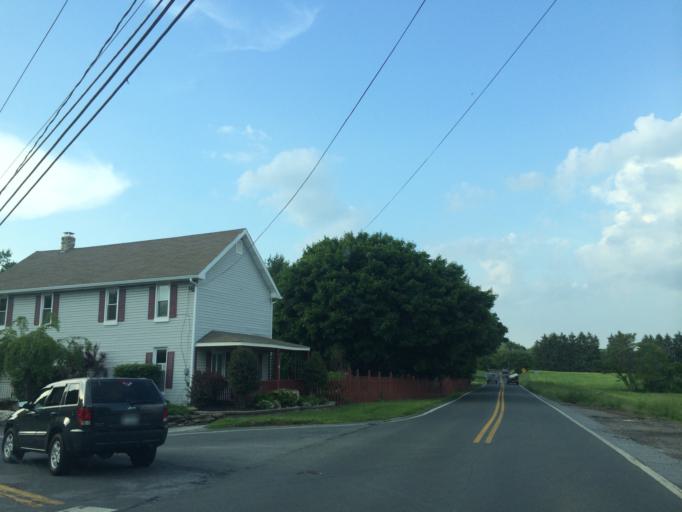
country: US
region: Maryland
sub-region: Carroll County
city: Eldersburg
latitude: 39.4506
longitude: -76.9897
